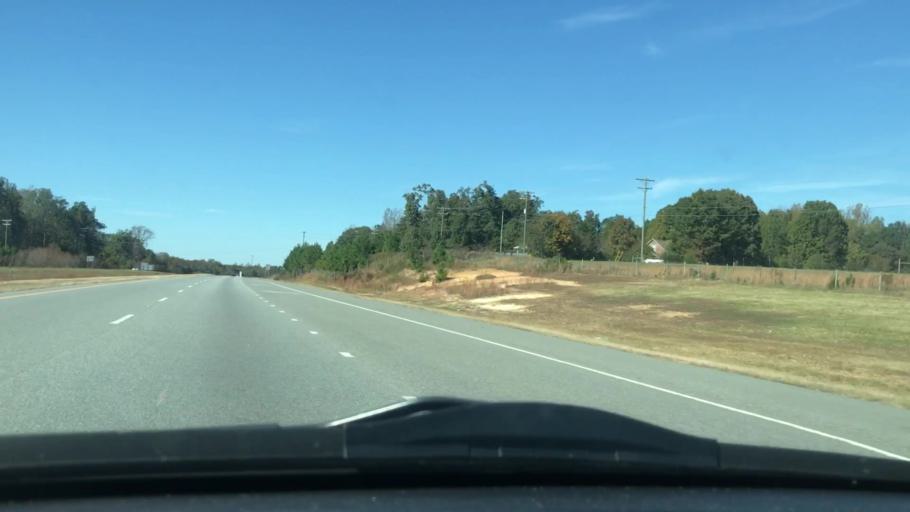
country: US
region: North Carolina
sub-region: Randolph County
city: Archdale
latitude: 35.8750
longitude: -79.9033
